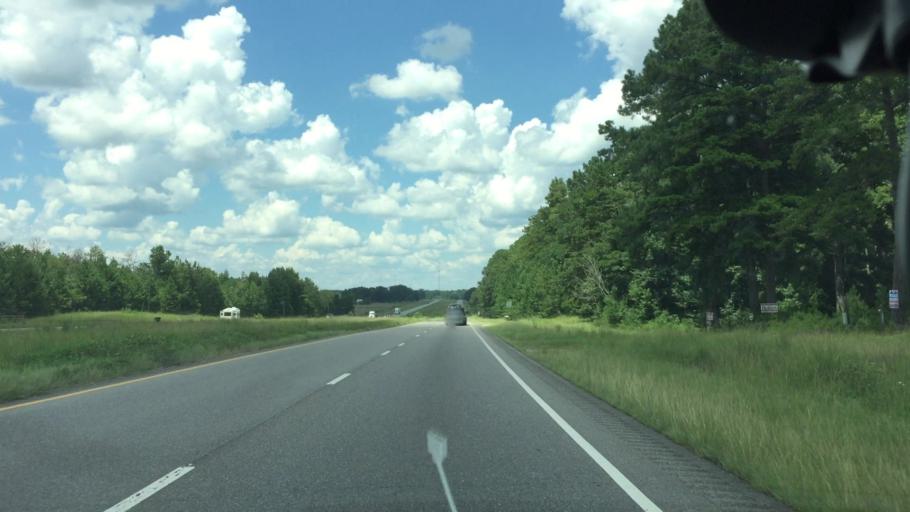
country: US
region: Alabama
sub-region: Montgomery County
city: Taylor
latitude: 32.0211
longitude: -86.0312
